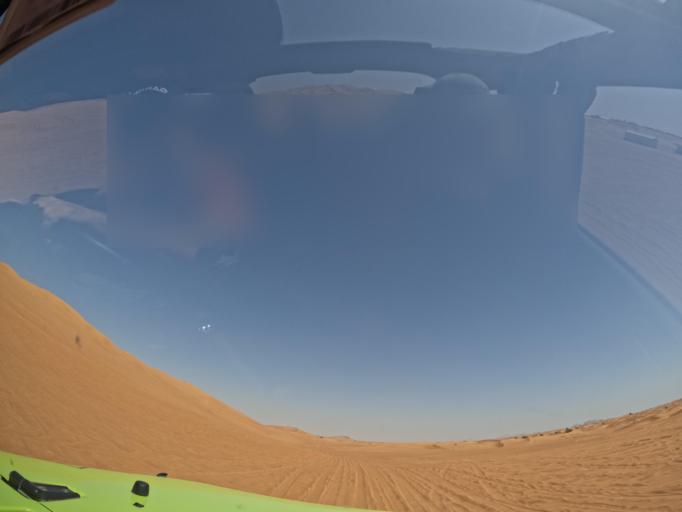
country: AE
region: Ash Shariqah
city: Adh Dhayd
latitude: 24.9595
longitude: 55.7201
